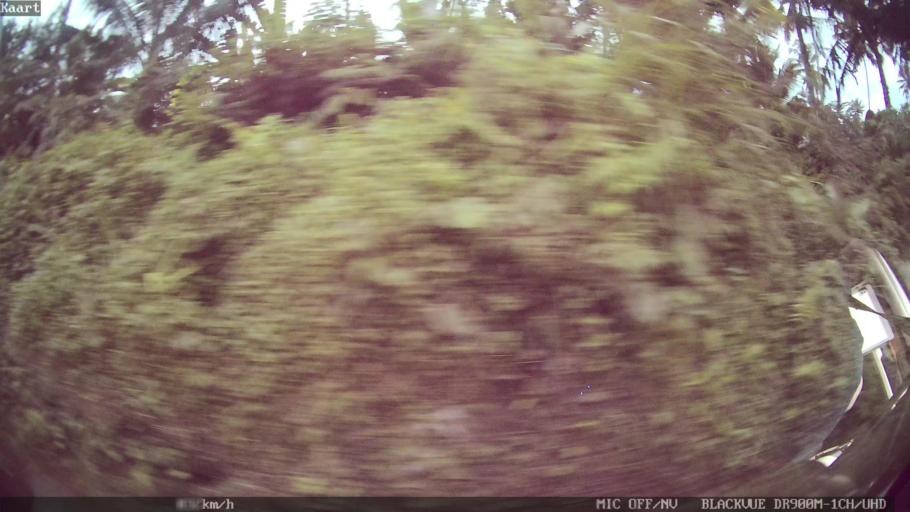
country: ID
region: Bali
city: Banjar Wangsian
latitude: -8.4585
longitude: 115.4141
